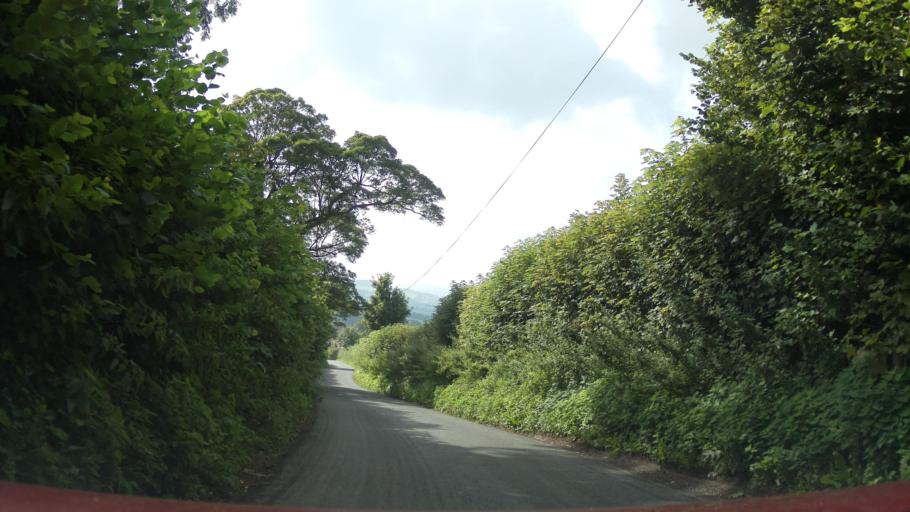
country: GB
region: England
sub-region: Somerset
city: Evercreech
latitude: 51.1639
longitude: -2.5056
